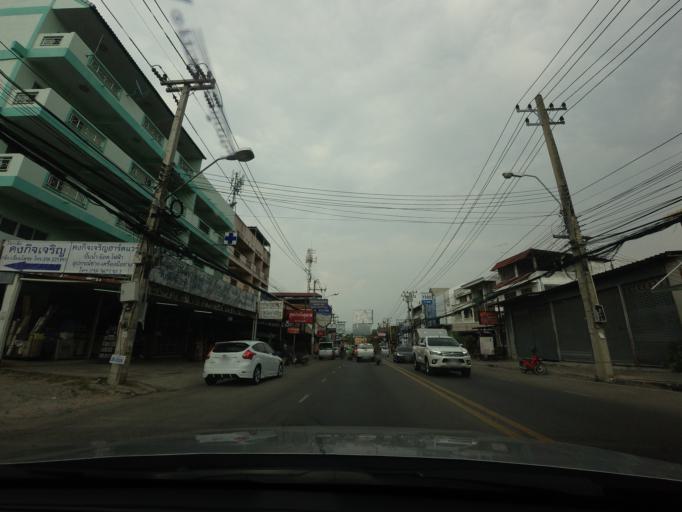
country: TH
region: Chon Buri
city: Phatthaya
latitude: 12.9674
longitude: 100.8995
